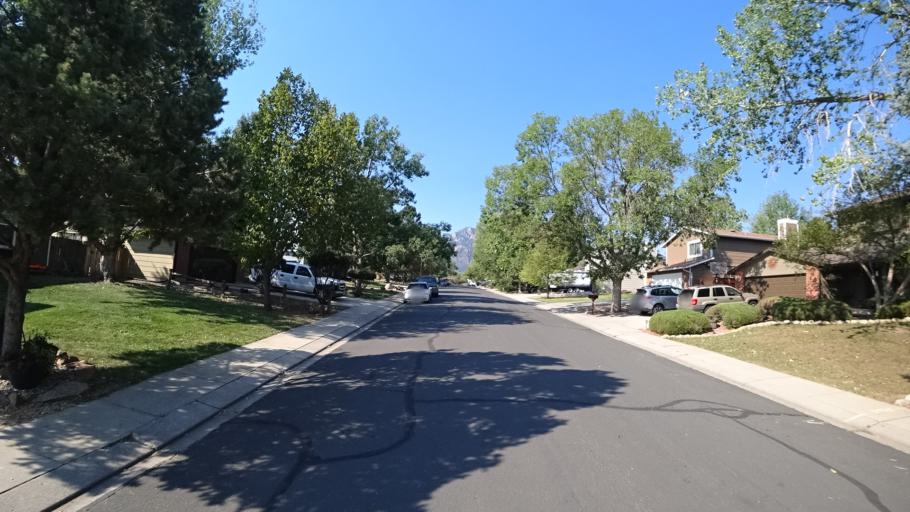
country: US
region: Colorado
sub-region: El Paso County
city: Stratmoor
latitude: 38.7836
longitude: -104.8150
